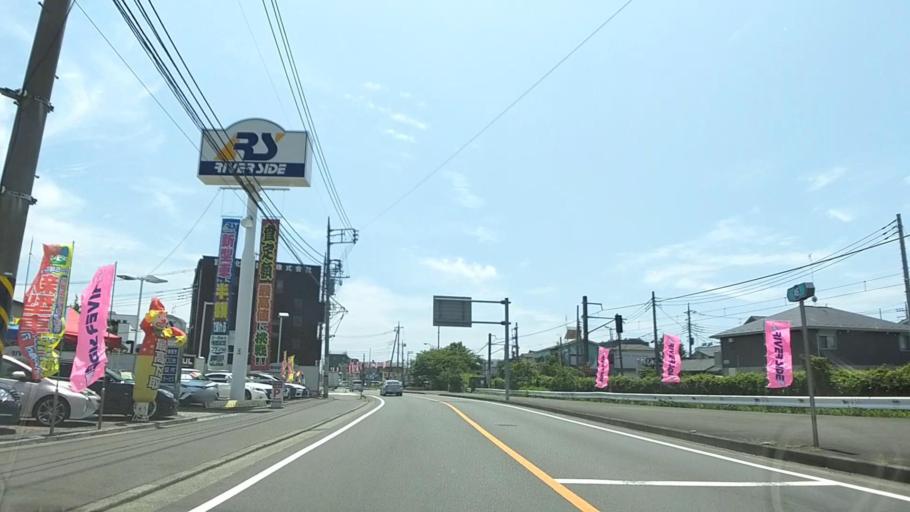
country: JP
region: Kanagawa
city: Atsugi
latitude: 35.4026
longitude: 139.3819
